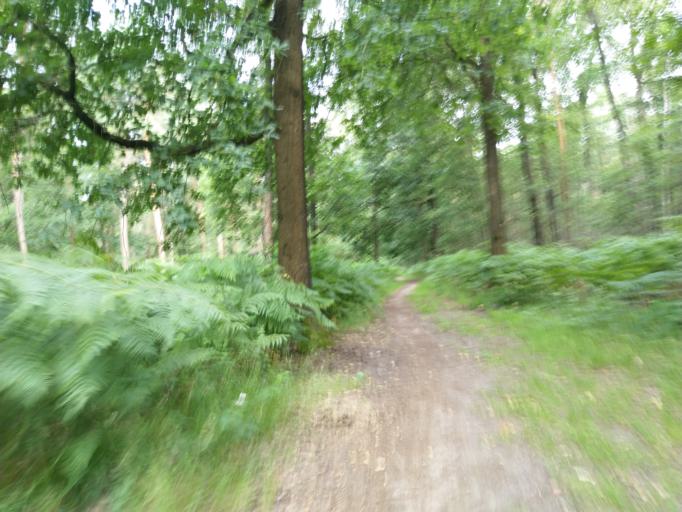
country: BE
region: Wallonia
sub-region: Province du Hainaut
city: Saint-Ghislain
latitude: 50.5005
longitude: 3.8382
